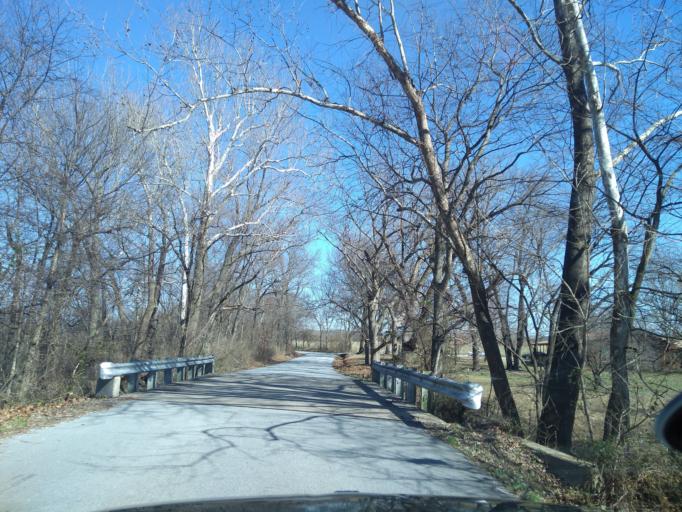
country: US
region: Arkansas
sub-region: Washington County
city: Farmington
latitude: 36.0610
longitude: -94.2518
